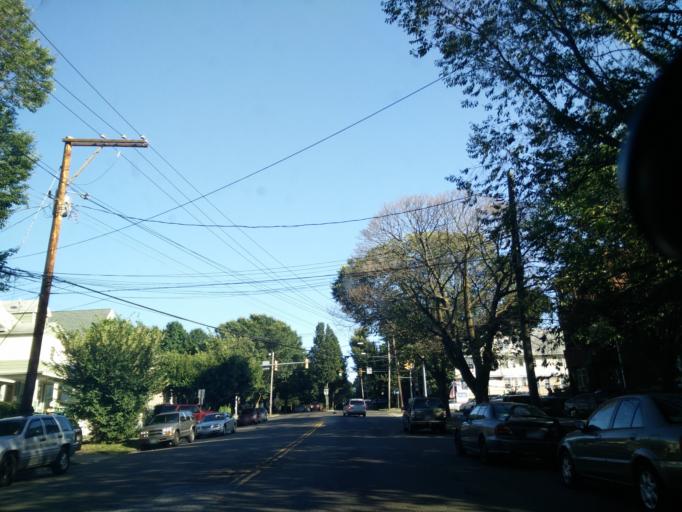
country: US
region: Connecticut
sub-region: Fairfield County
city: Bridgeport
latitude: 41.1816
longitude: -73.2052
